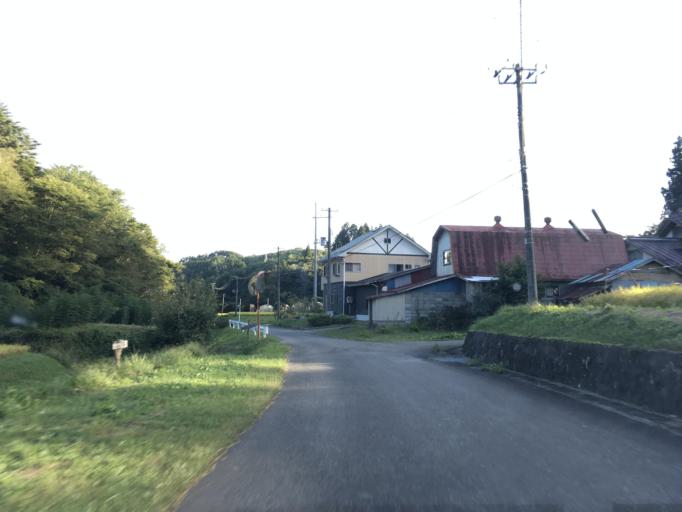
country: JP
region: Iwate
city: Ichinoseki
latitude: 38.7946
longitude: 141.4207
